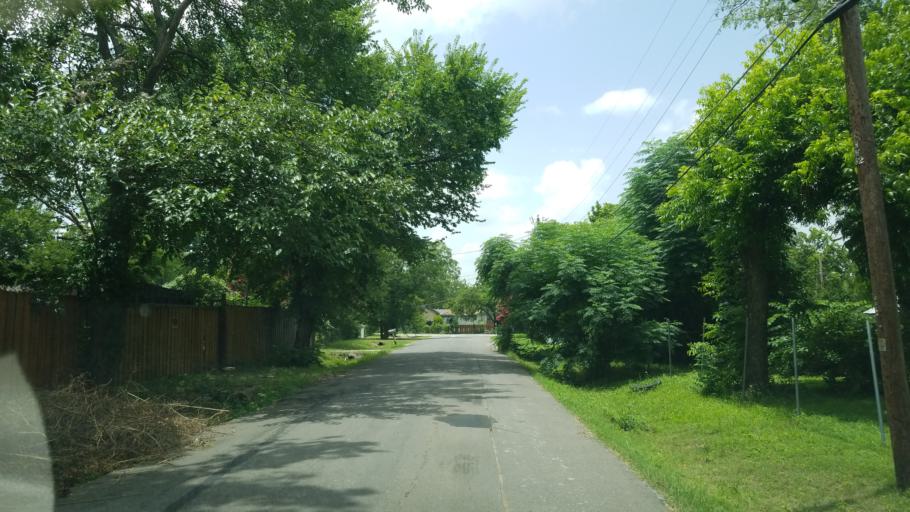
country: US
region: Texas
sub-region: Dallas County
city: Cockrell Hill
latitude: 32.7809
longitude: -96.8994
